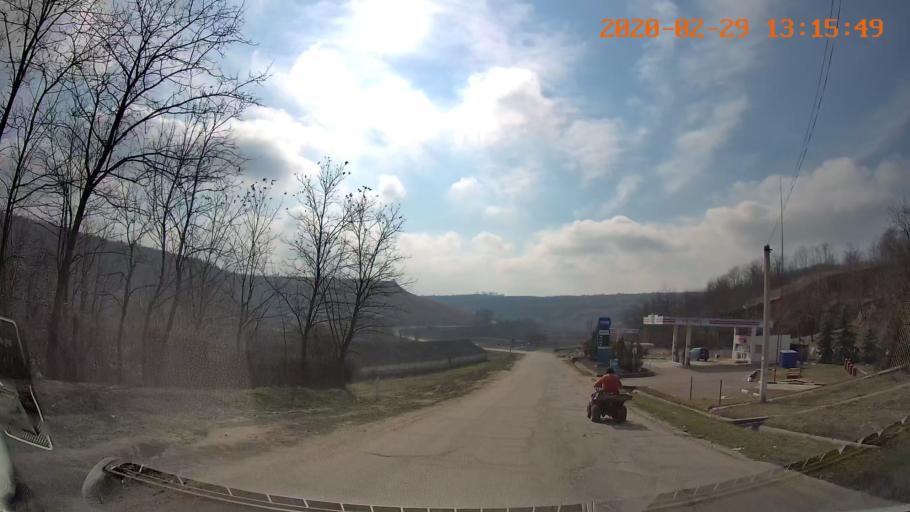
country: MD
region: Telenesti
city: Camenca
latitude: 48.0073
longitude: 28.6679
